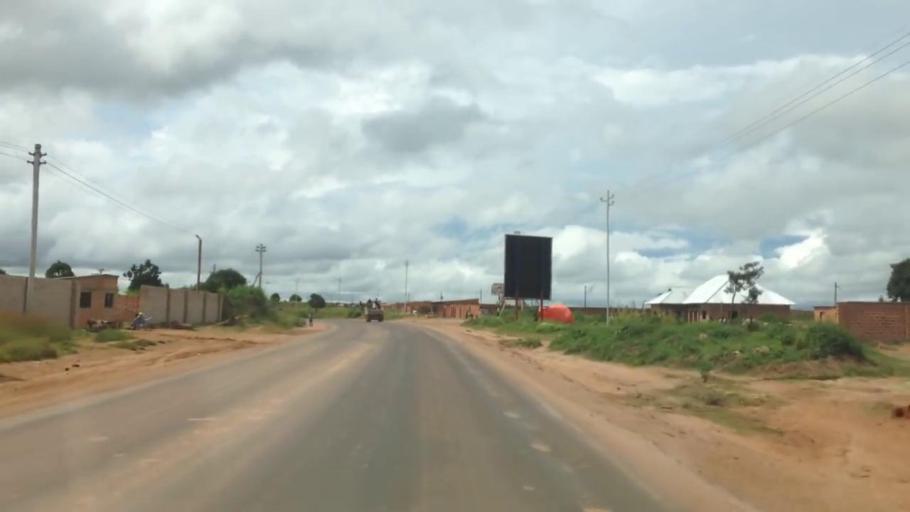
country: CD
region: Katanga
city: Kolwezi
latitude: -10.7401
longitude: 25.5122
